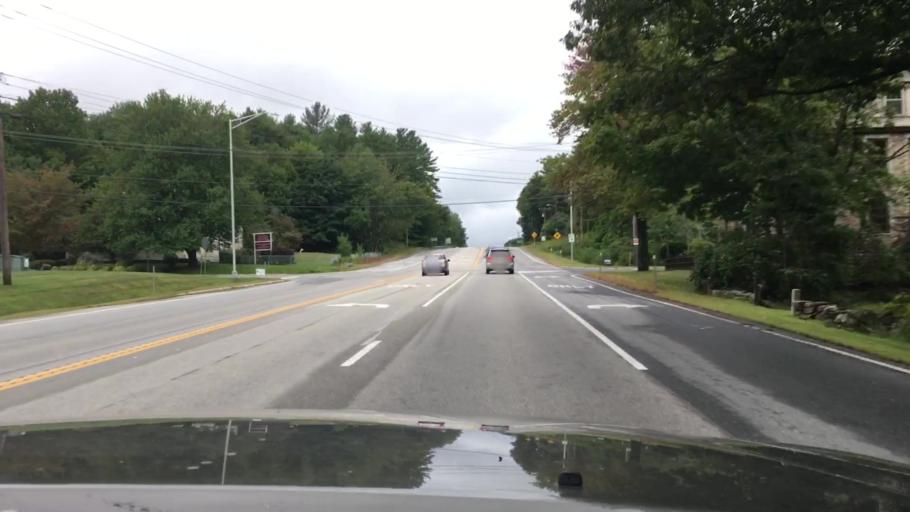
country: US
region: New Hampshire
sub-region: Cheshire County
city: Chesterfield
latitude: 42.9009
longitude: -72.4591
